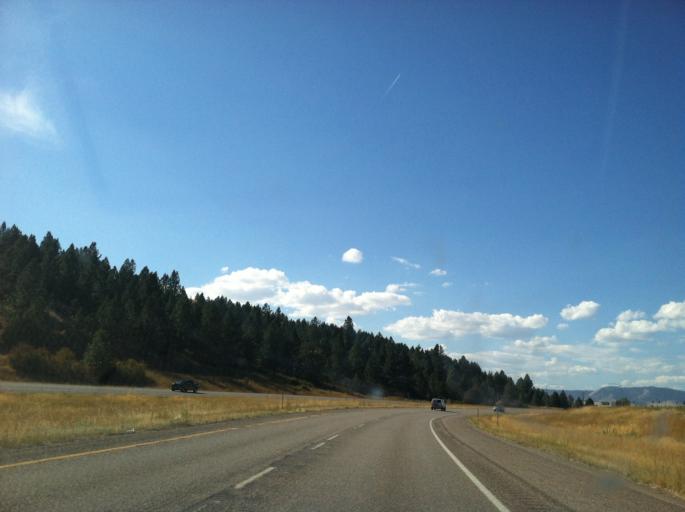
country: US
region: Montana
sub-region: Lake County
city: Polson
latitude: 47.6792
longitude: -114.1153
